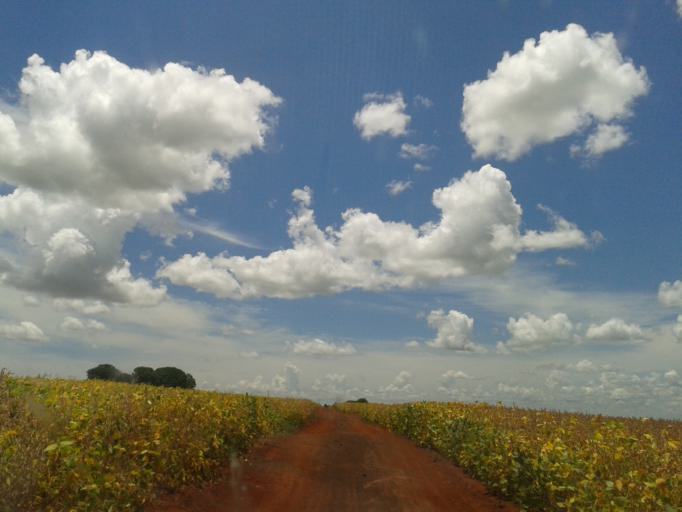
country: BR
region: Minas Gerais
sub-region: Capinopolis
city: Capinopolis
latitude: -18.7648
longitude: -49.7947
